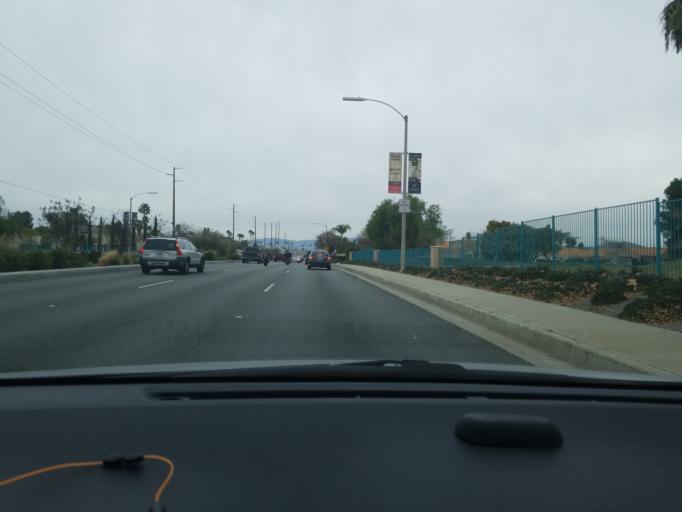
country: US
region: California
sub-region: Riverside County
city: Sun City
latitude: 33.6852
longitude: -117.1640
